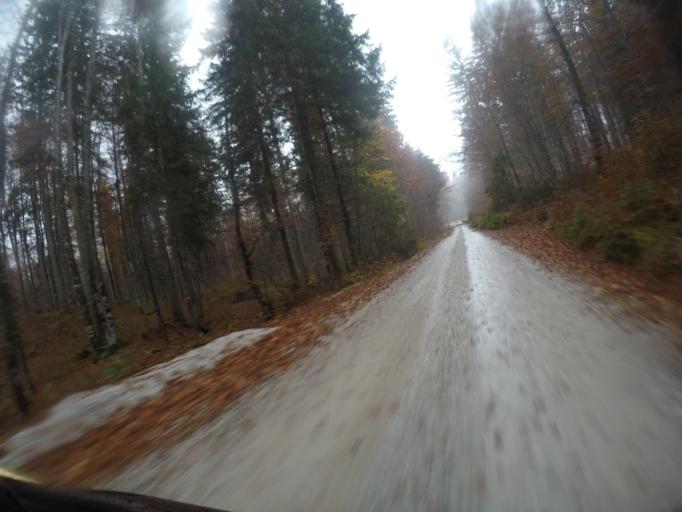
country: SI
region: Kranjska Gora
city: Mojstrana
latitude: 46.4241
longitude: 13.8651
